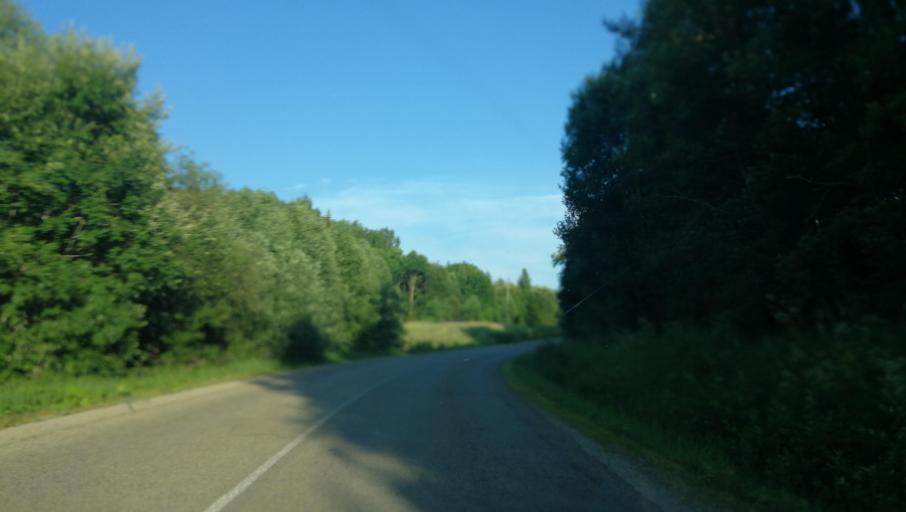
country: LV
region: Priekuli
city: Priekuli
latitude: 57.2589
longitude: 25.3666
